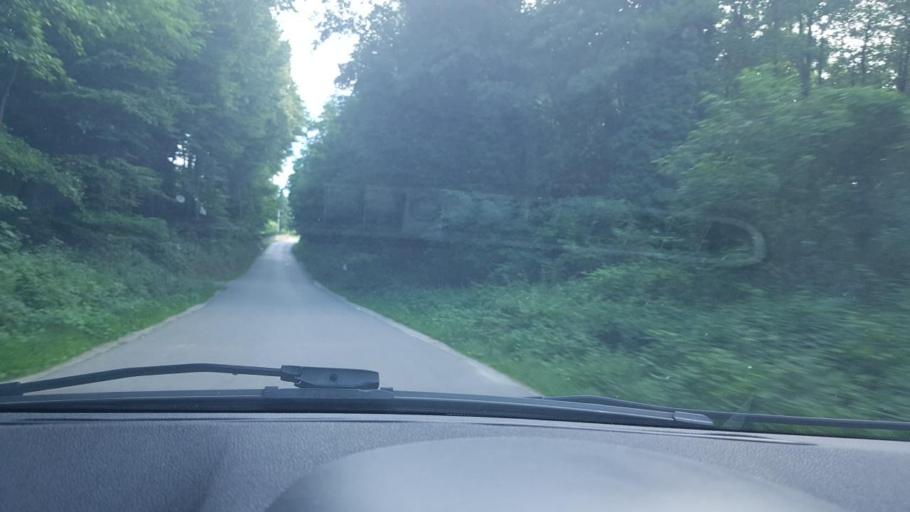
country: HR
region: Varazdinska
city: Tuzno
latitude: 46.2637
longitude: 16.1879
